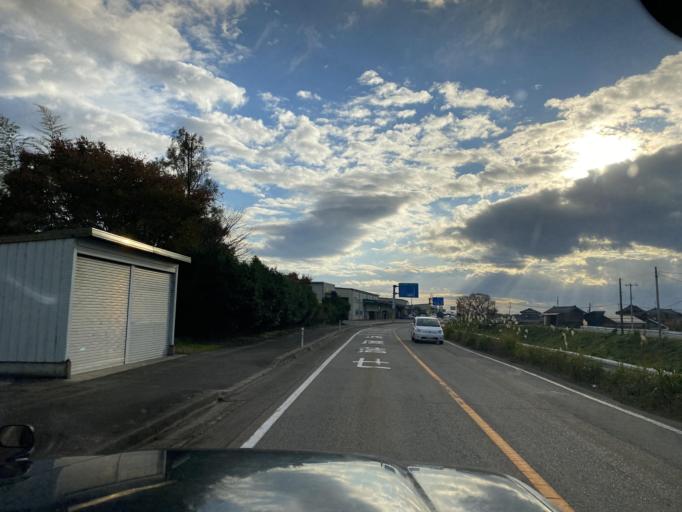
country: JP
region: Niigata
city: Kamo
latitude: 37.6815
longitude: 139.0197
